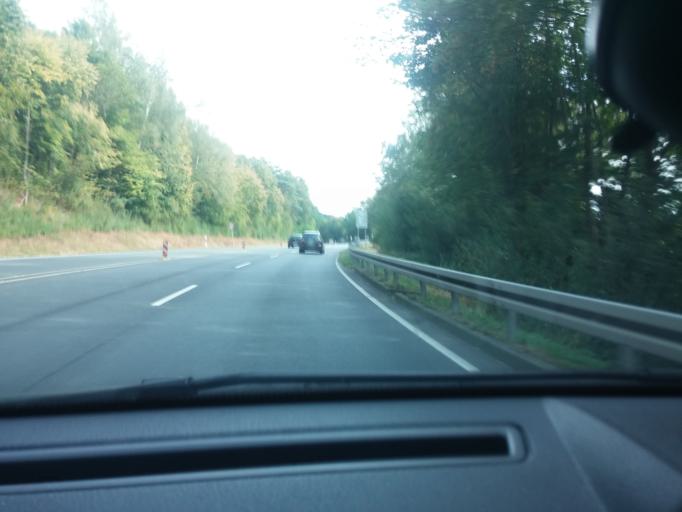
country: DE
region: Hesse
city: Hochst im Odenwald
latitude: 49.8267
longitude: 8.9599
